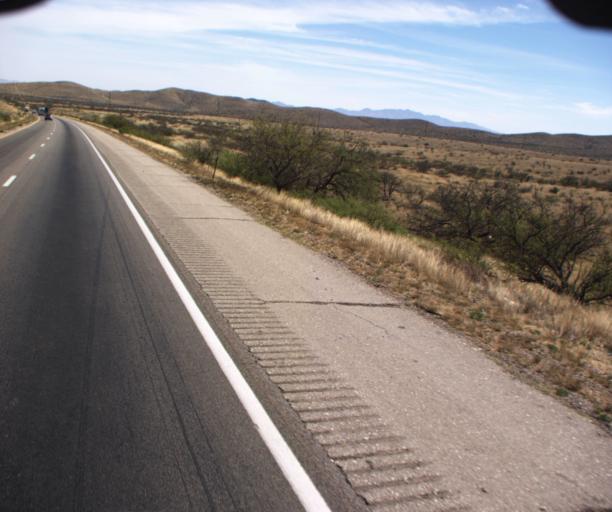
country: US
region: Arizona
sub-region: Cochise County
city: Saint David
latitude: 32.0899
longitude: -110.0390
